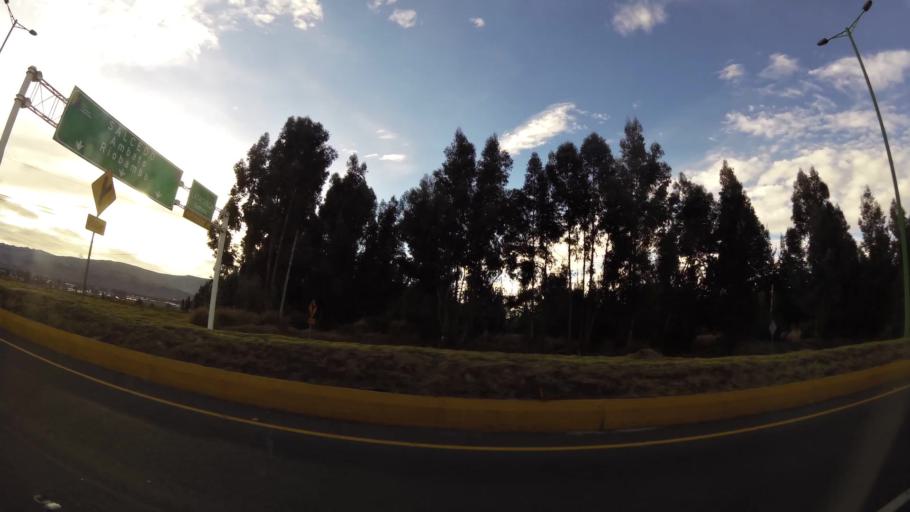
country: EC
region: Cotopaxi
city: Saquisili
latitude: -0.8615
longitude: -78.6240
